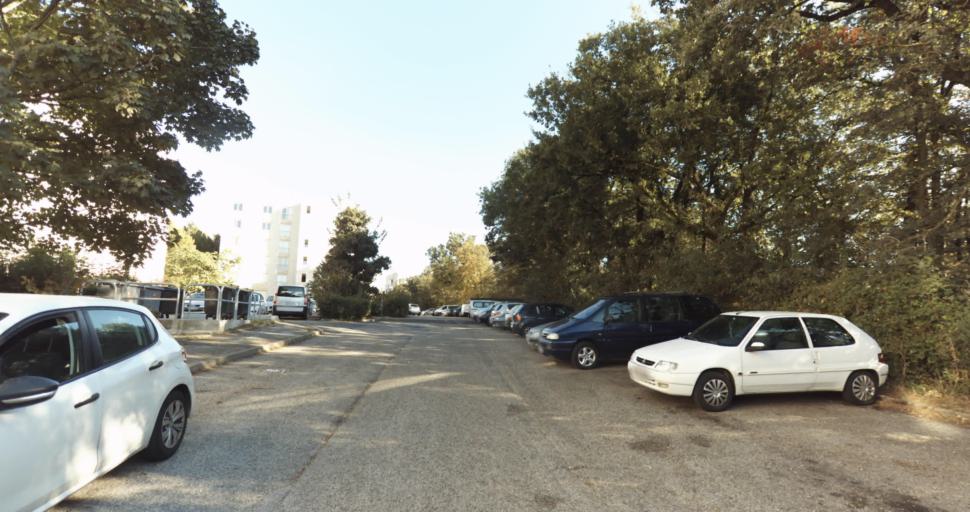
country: FR
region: Rhone-Alpes
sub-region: Departement du Rhone
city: Neuville-sur-Saone
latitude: 45.8811
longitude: 4.8452
